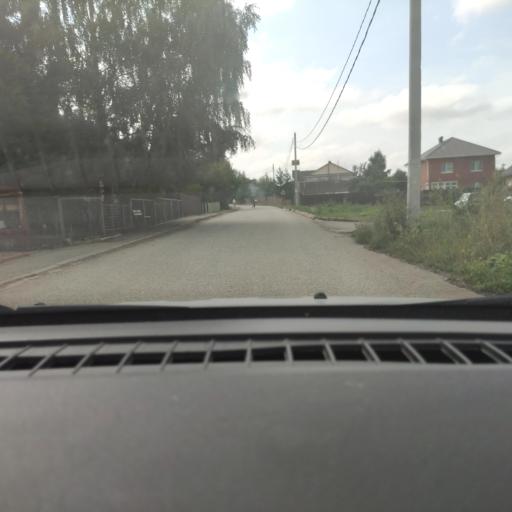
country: RU
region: Perm
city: Lobanovo
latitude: 57.8624
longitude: 56.2812
